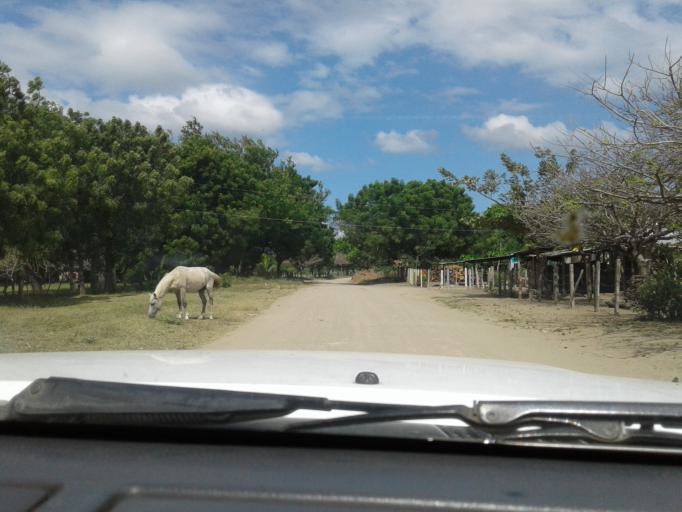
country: NI
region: Rivas
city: Belen
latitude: 11.6467
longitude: -85.8666
